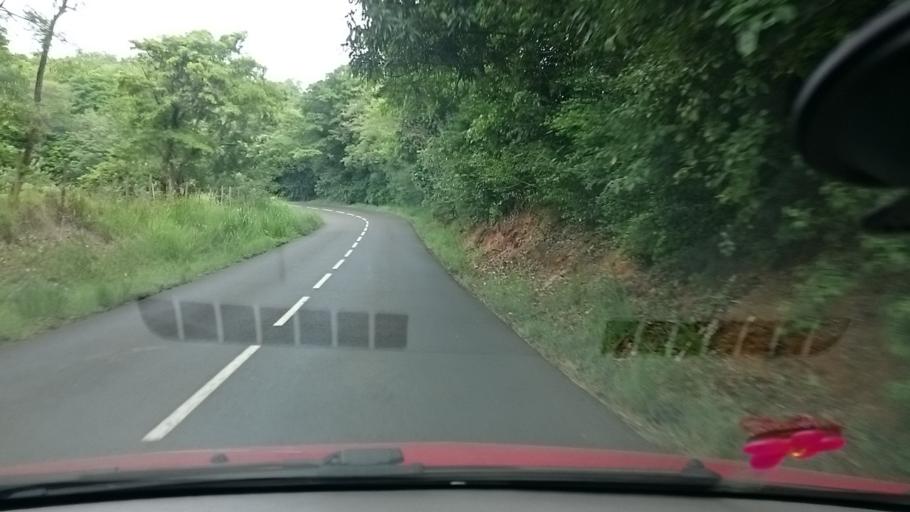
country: MQ
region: Martinique
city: Petite Riviere Salee
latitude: 14.7569
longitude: -60.9357
